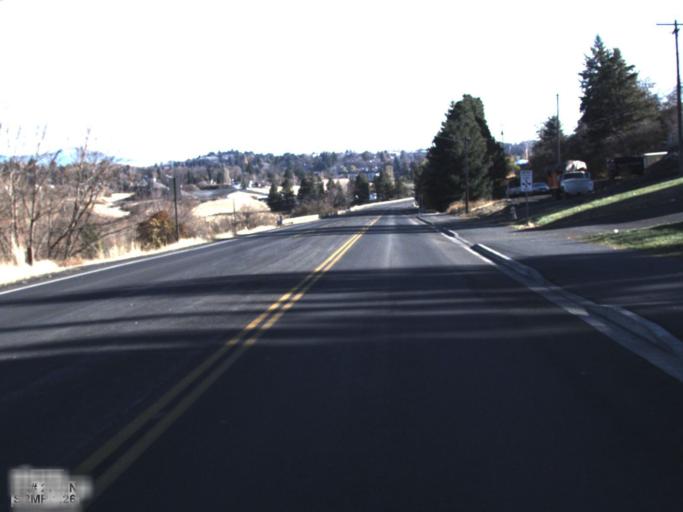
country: US
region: Washington
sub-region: Whitman County
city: Pullman
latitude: 46.7338
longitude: -117.2002
